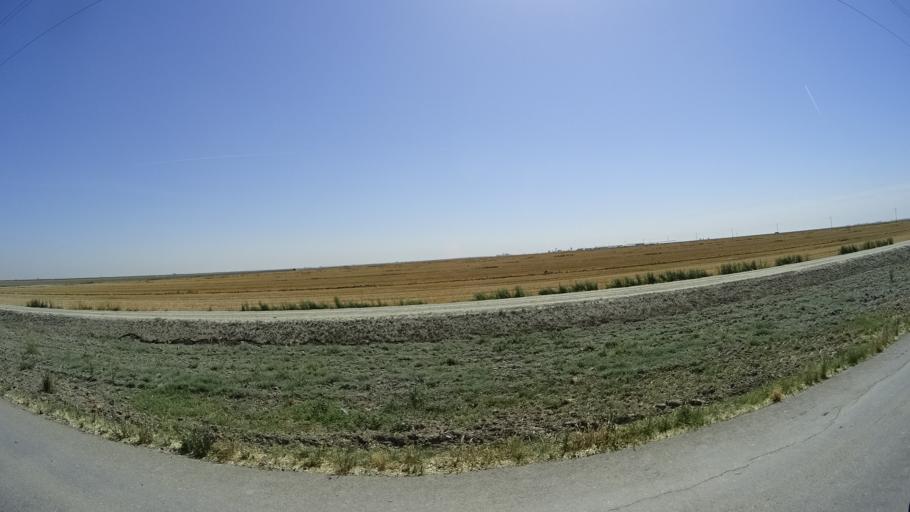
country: US
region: California
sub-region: Kings County
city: Corcoran
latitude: 35.9963
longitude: -119.5362
